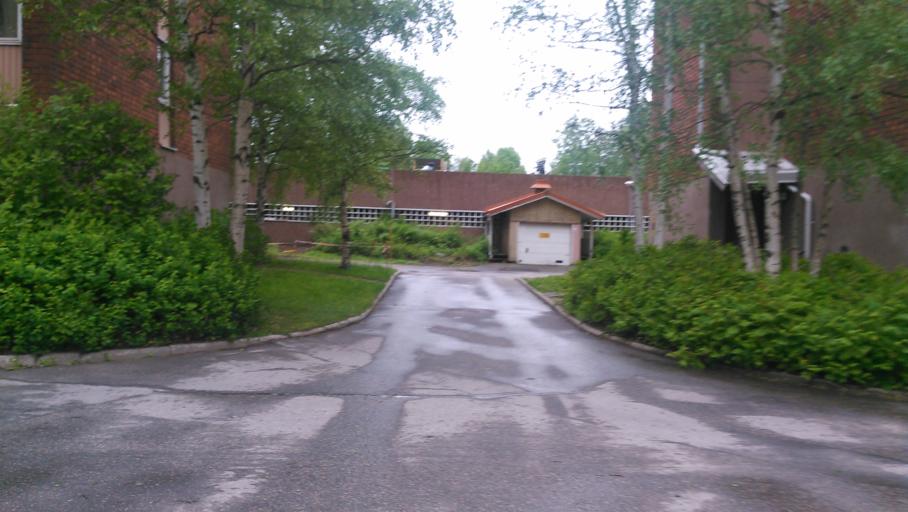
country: SE
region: Vaesterbotten
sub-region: Umea Kommun
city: Umea
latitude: 63.8128
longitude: 20.3073
